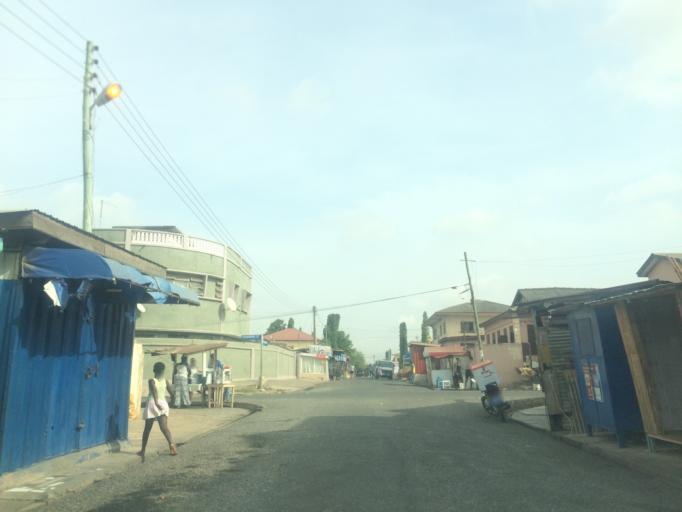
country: GH
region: Greater Accra
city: Accra
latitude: 5.5632
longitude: -0.2102
